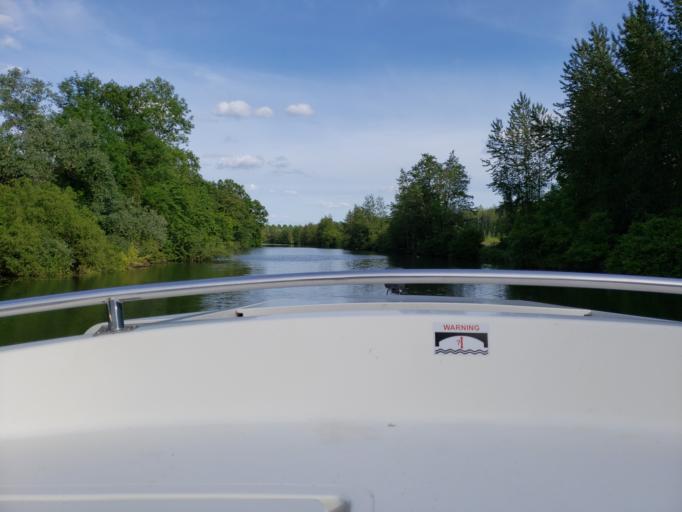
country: FR
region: Bourgogne
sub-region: Departement de l'Yonne
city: Migennes
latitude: 47.9440
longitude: 3.5050
